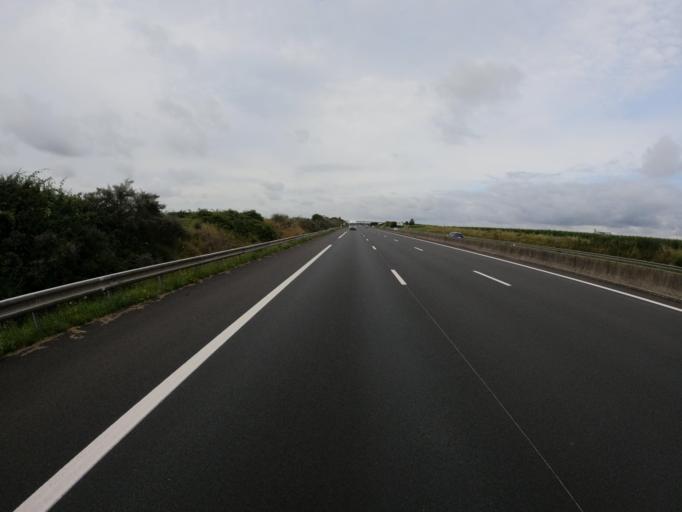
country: FR
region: Centre
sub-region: Departement d'Indre-et-Loire
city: Auzouer-en-Touraine
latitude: 47.5525
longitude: 1.0058
